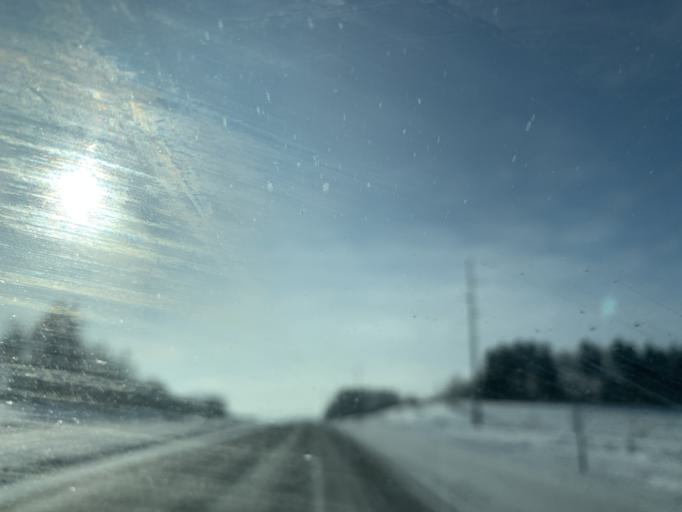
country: US
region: Minnesota
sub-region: Dakota County
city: Lakeville
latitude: 44.6725
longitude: -93.2174
